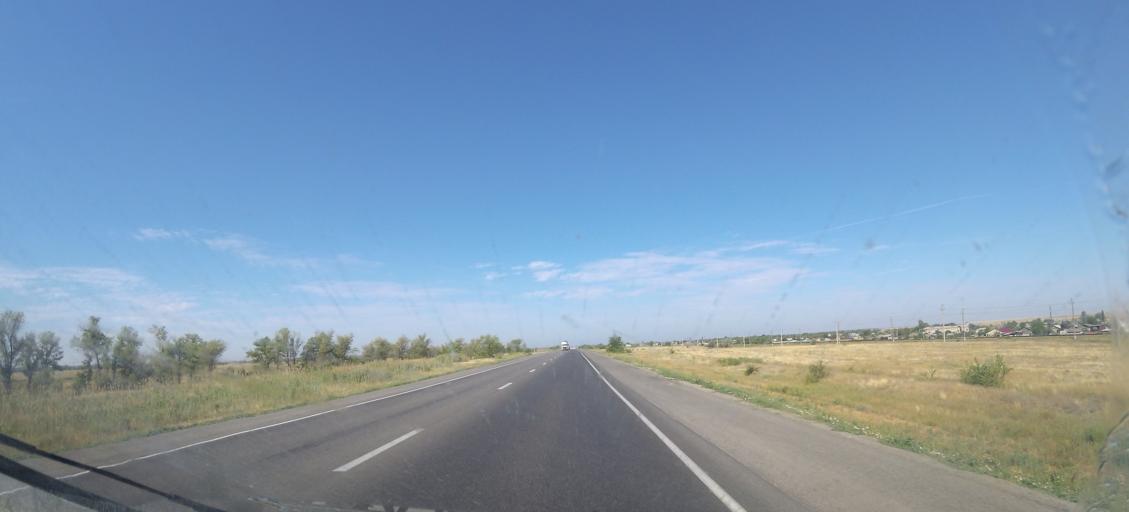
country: RU
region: Volgograd
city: Oktyabr'skiy
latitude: 48.6833
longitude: 43.9259
